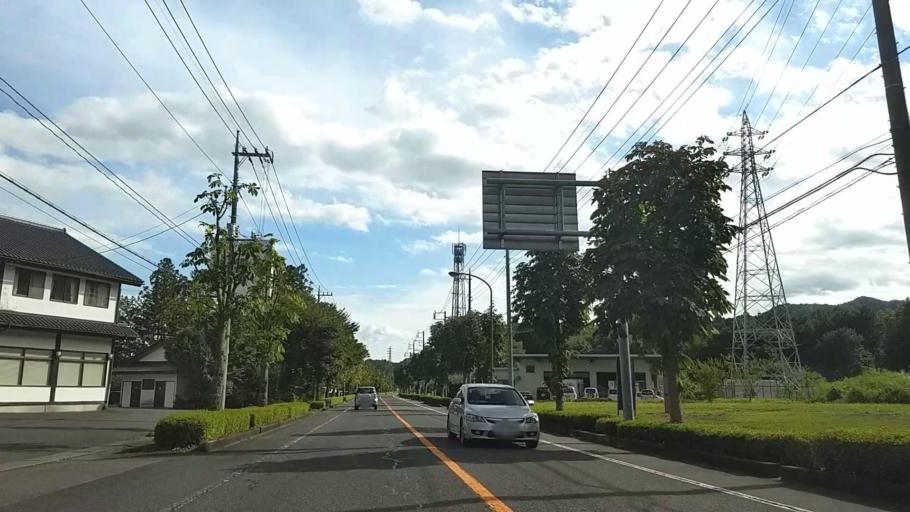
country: JP
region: Tochigi
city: Imaichi
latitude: 36.7921
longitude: 139.7017
